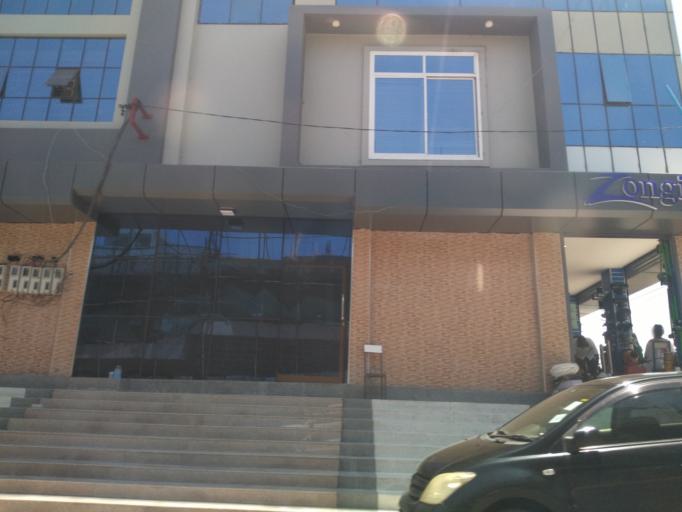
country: TZ
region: Mwanza
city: Mwanza
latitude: -2.5245
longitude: 32.9021
